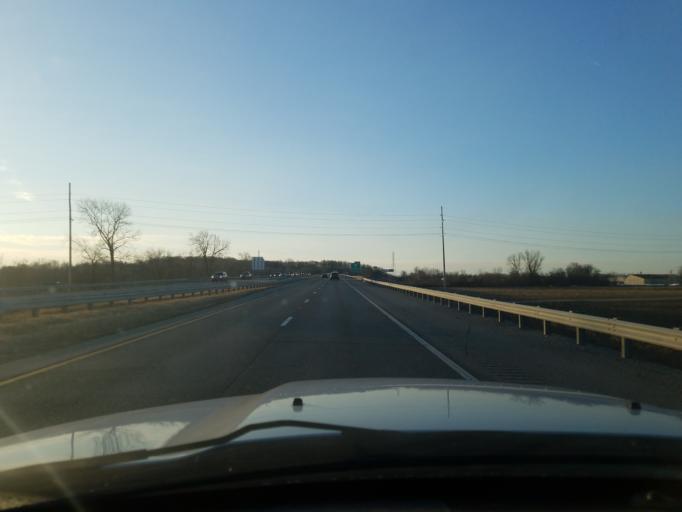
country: US
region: Kentucky
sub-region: Henderson County
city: Henderson
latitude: 37.8433
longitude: -87.5658
